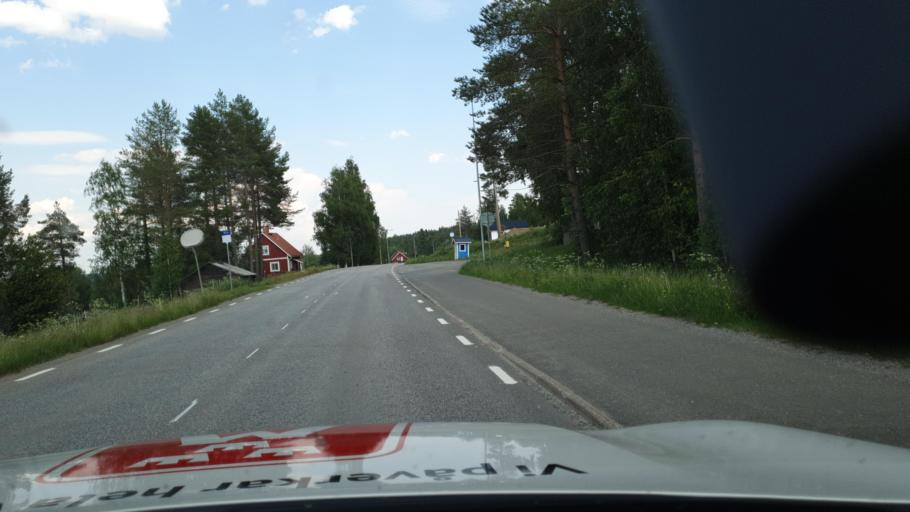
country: SE
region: Vaesterbotten
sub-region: Skelleftea Kommun
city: Viken
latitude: 64.7331
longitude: 20.7384
